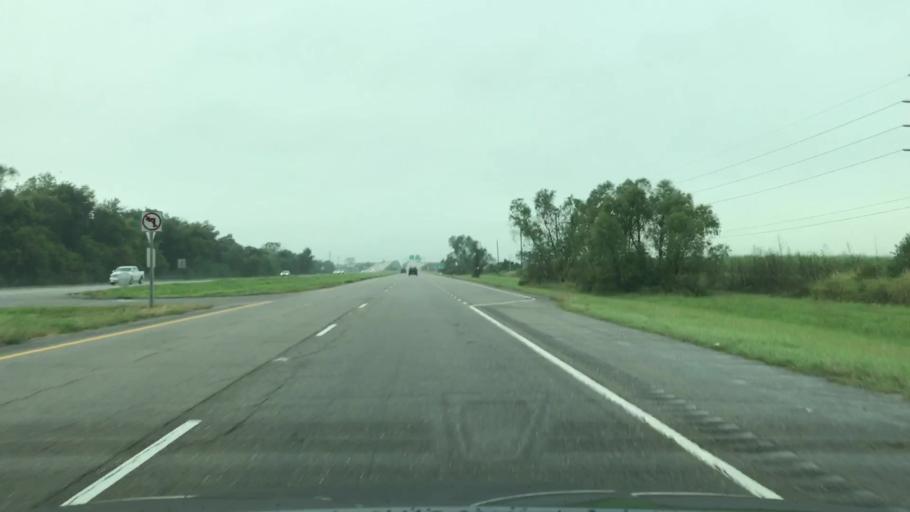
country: US
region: Louisiana
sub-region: Lafourche Parish
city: Mathews
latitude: 29.7175
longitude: -90.5635
